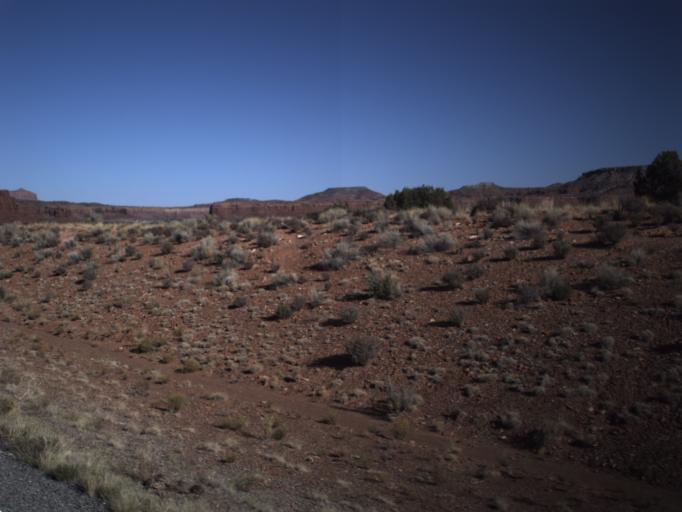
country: US
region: Utah
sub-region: San Juan County
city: Blanding
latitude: 37.6777
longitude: -110.2136
